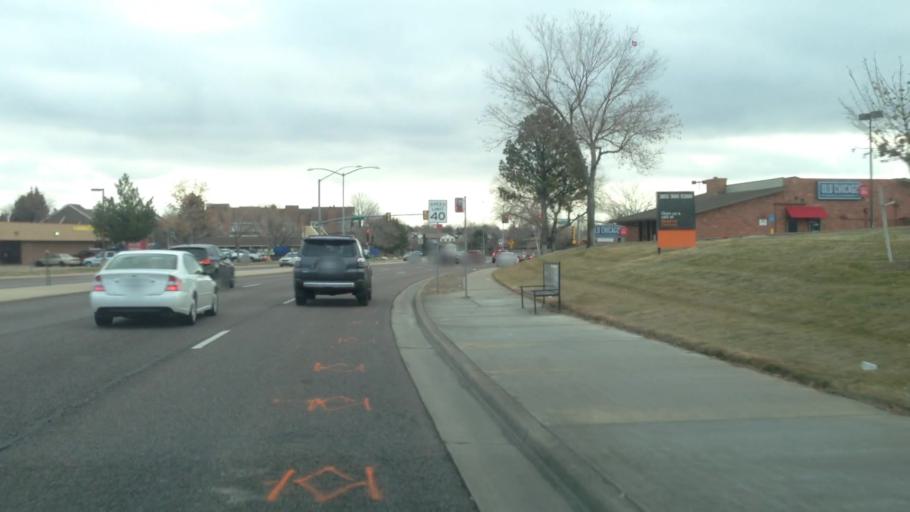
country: US
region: Colorado
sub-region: Adams County
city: Aurora
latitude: 39.6735
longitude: -104.7906
